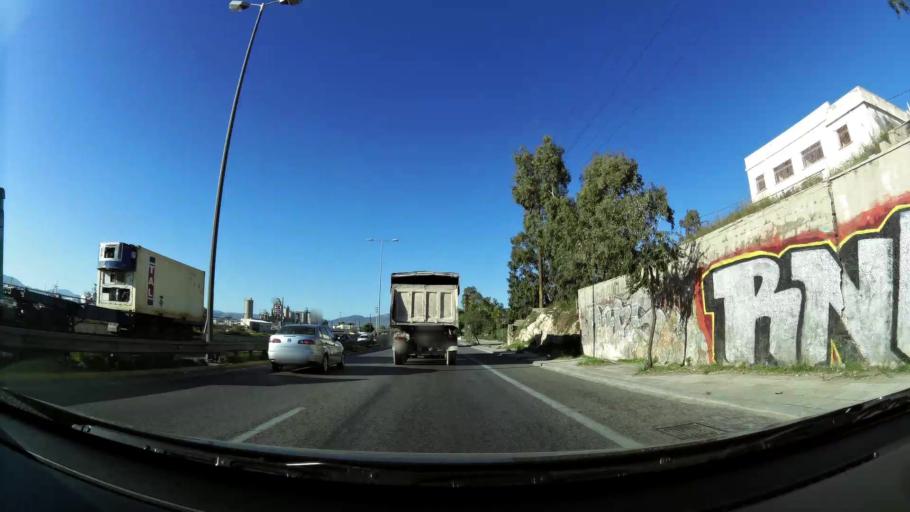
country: GR
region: Attica
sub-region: Nomarchia Athinas
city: Skaramangas
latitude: 38.0275
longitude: 23.5982
